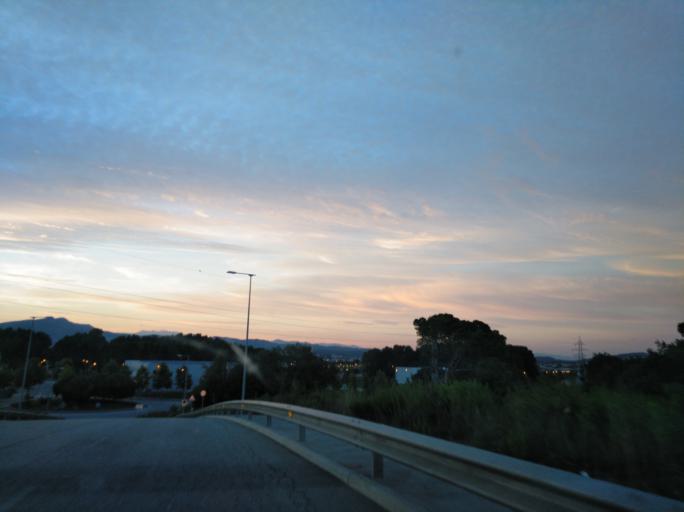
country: ES
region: Catalonia
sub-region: Provincia de Girona
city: Fornells de la Selva
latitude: 41.9446
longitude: 2.7997
